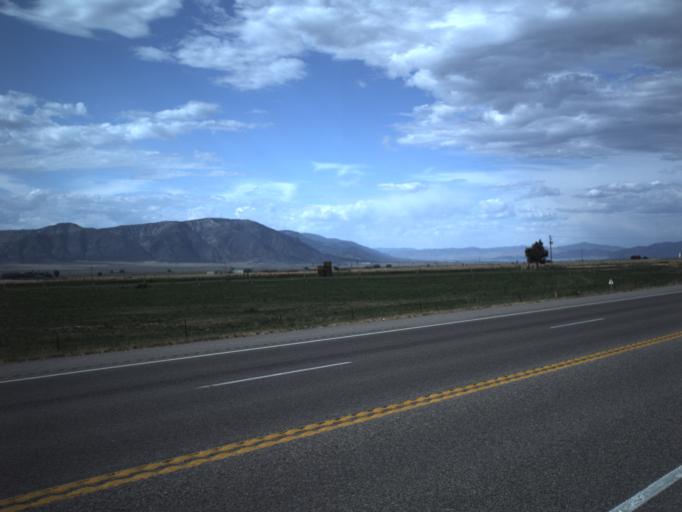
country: US
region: Utah
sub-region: Sanpete County
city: Ephraim
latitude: 39.3156
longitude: -111.6091
